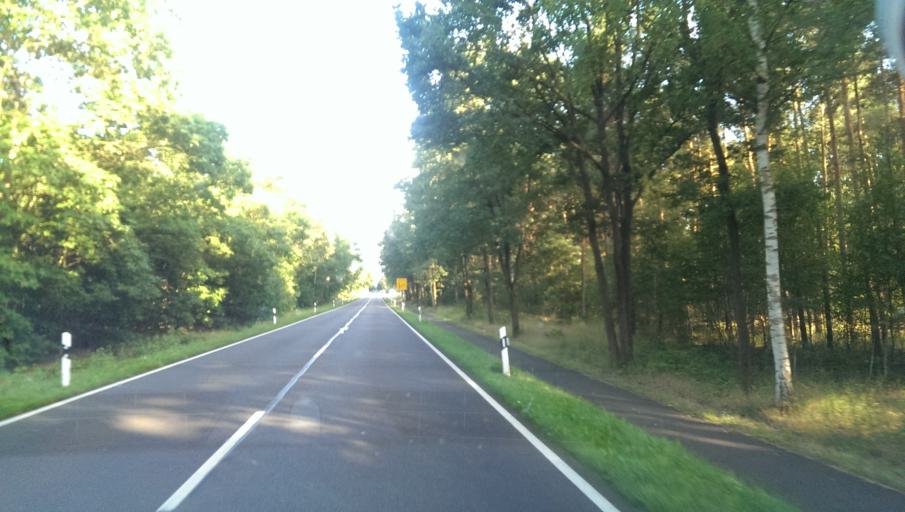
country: DE
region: Brandenburg
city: Treuenbrietzen
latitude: 52.0588
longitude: 12.9021
